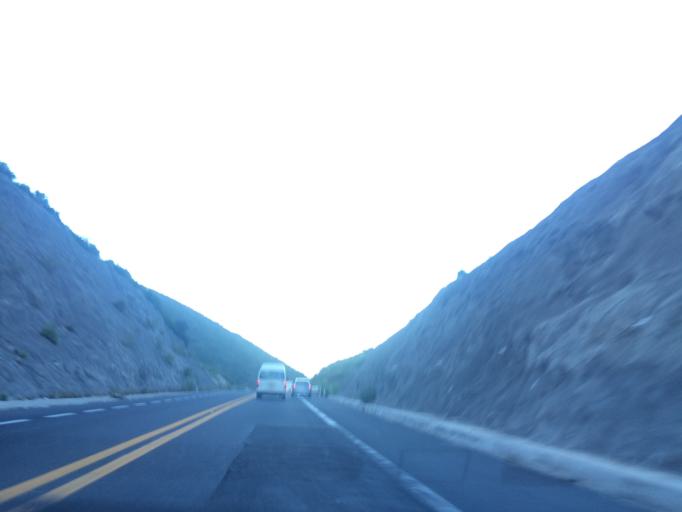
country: MX
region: Puebla
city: Chapuco
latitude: 18.6505
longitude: -97.4527
